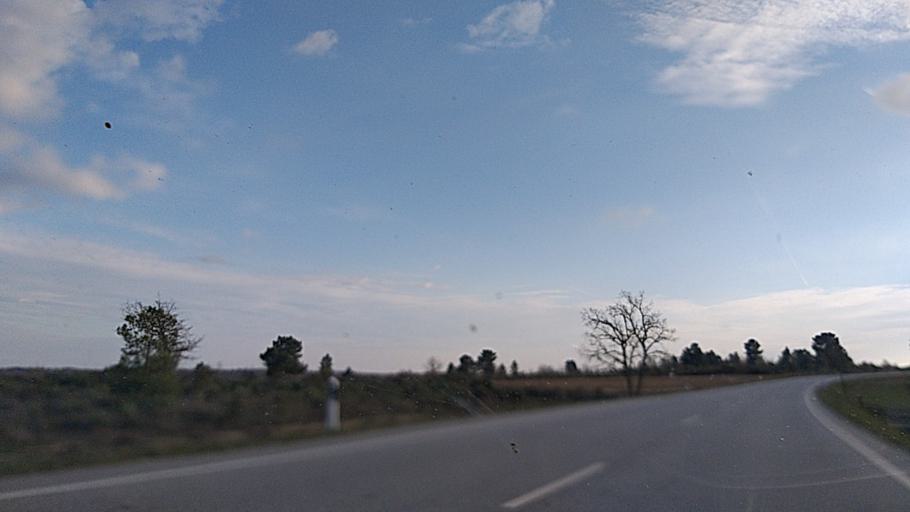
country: ES
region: Castille and Leon
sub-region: Provincia de Salamanca
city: Fuentes de Onoro
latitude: 40.6288
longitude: -6.9734
